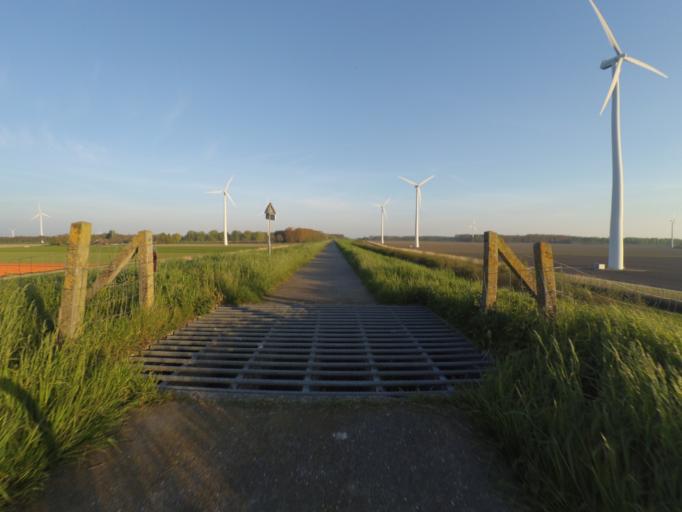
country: NL
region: Flevoland
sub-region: Gemeente Zeewolde
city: Zeewolde
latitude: 52.3961
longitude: 5.5130
